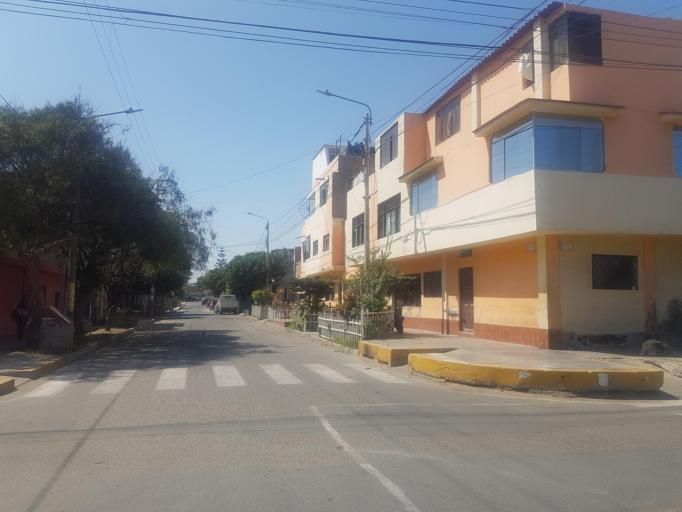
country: PE
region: Ancash
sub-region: Provincia de Santa
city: Chimbote
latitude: -9.0925
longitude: -78.5720
